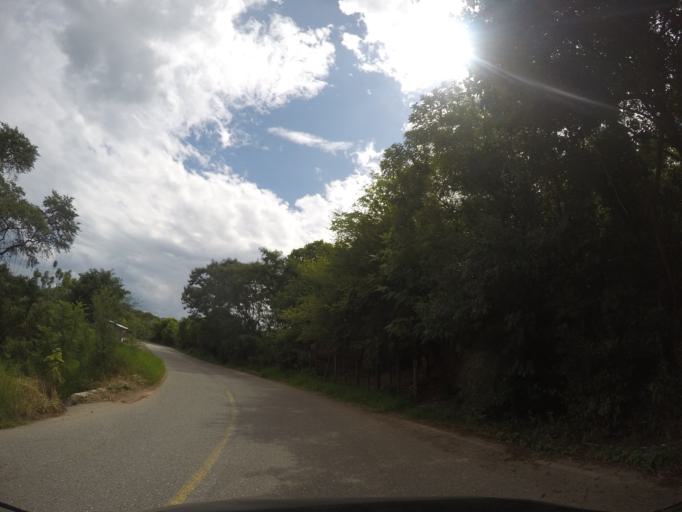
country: MX
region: Oaxaca
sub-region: San Jeronimo Coatlan
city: San Cristobal Honduras
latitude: 16.4323
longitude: -97.0652
